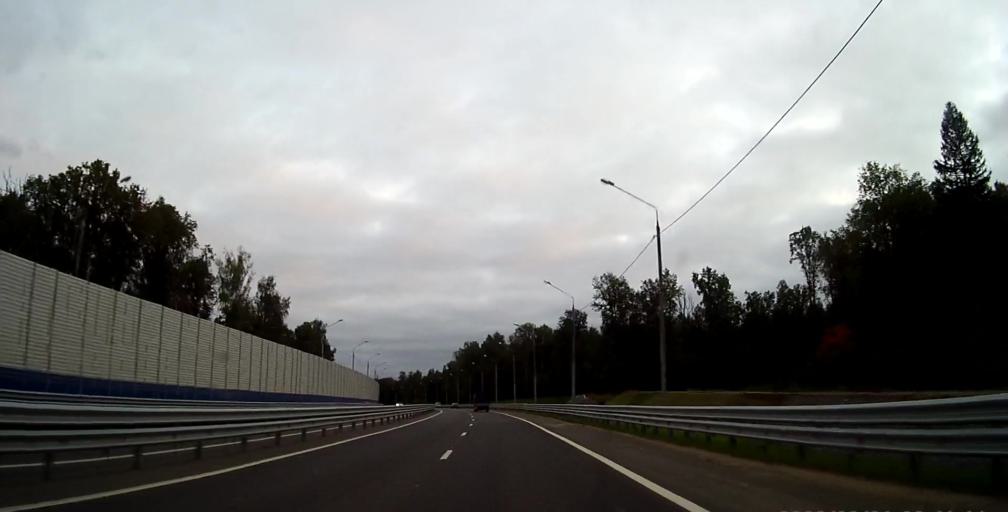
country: RU
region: Moskovskaya
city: Dubrovitsy
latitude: 55.4041
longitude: 37.5005
